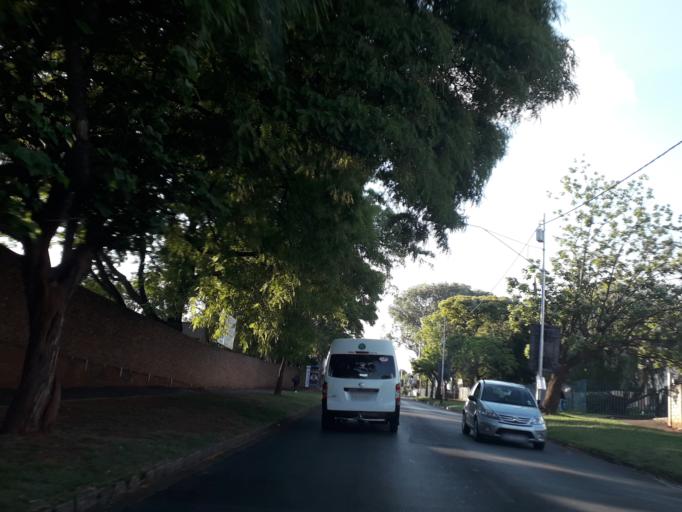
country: ZA
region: Gauteng
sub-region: City of Johannesburg Metropolitan Municipality
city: Johannesburg
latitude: -26.1381
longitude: 27.9960
